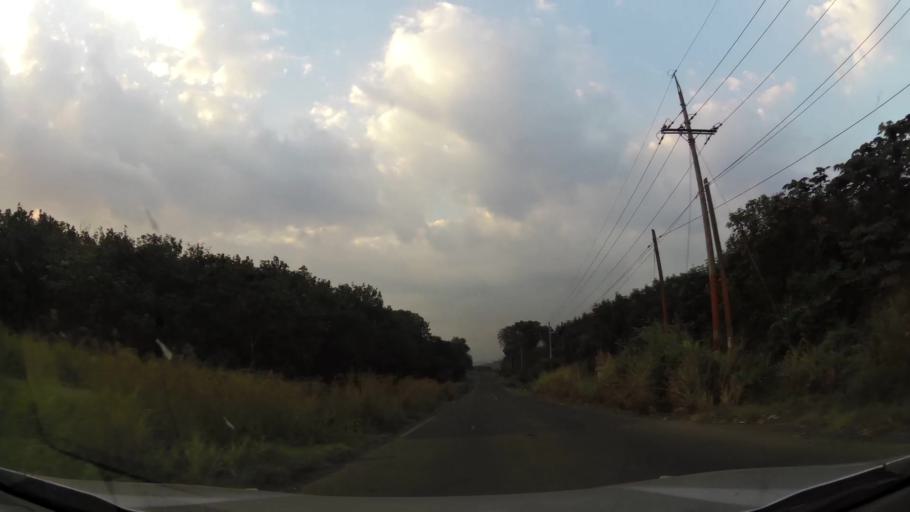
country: GT
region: Escuintla
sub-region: Municipio de La Democracia
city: La Democracia
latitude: 14.2689
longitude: -90.8975
